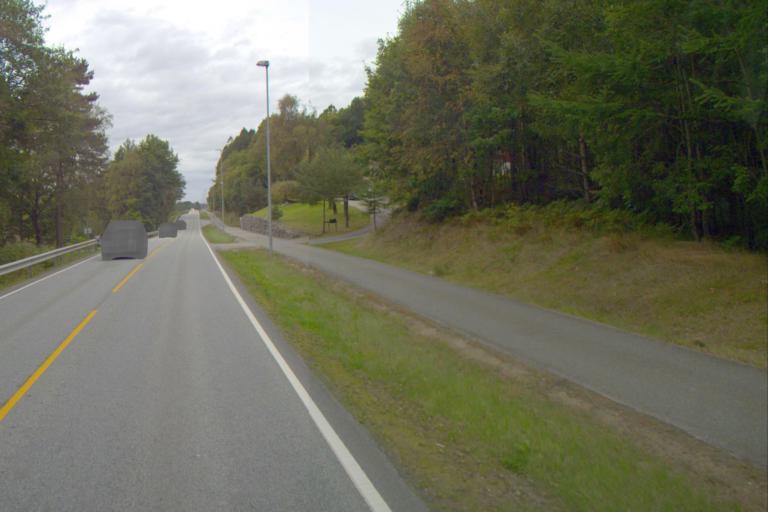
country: NO
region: Rogaland
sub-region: Sandnes
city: Hommersak
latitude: 58.8789
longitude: 5.8296
